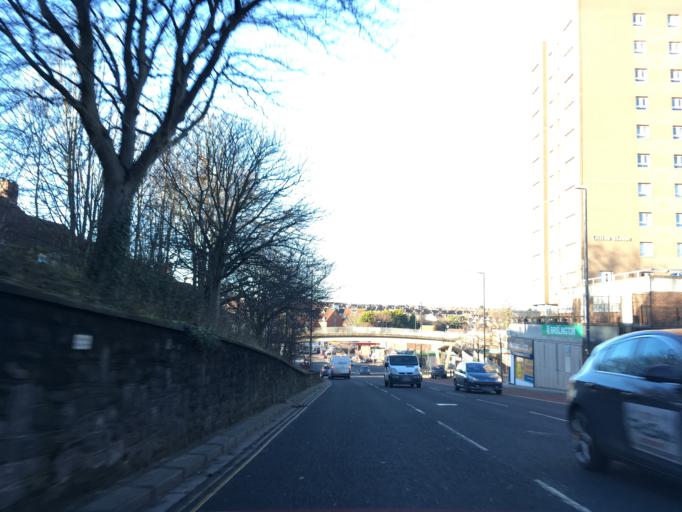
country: GB
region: England
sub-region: Bath and North East Somerset
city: Whitchurch
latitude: 51.4327
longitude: -2.5463
